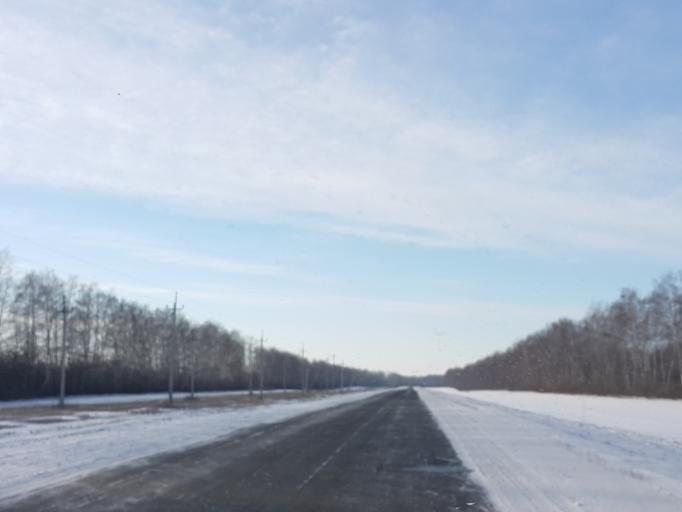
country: RU
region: Tambov
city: Znamenka
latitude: 52.3877
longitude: 41.3436
